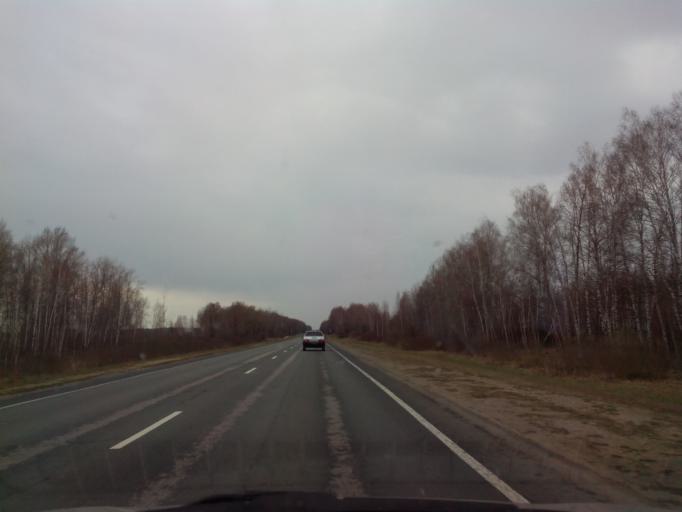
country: RU
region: Tambov
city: Michurinsk
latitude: 53.0581
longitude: 40.4551
